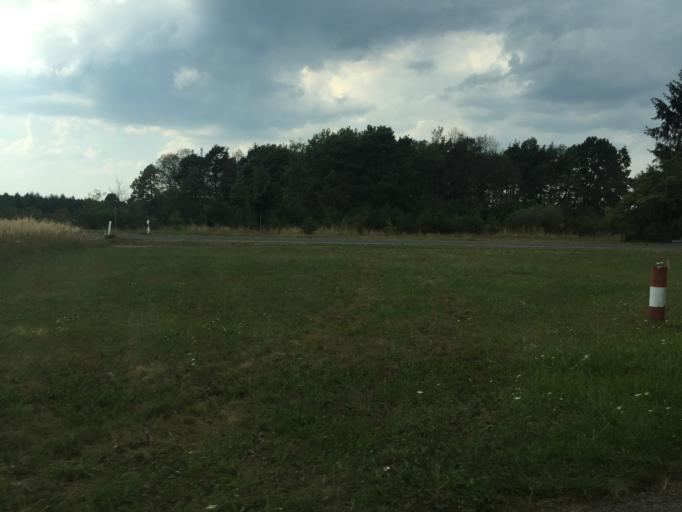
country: DE
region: Saxony
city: Schleife
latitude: 51.5277
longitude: 14.5280
